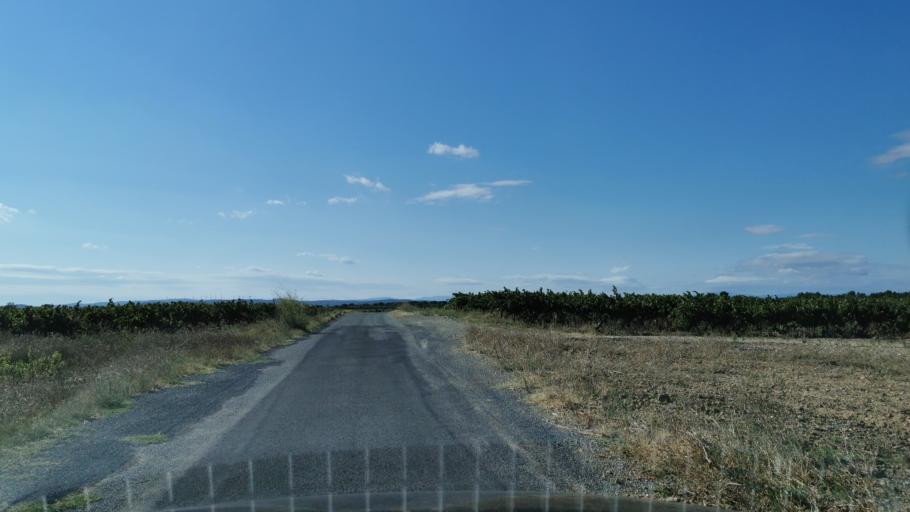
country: FR
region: Languedoc-Roussillon
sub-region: Departement de l'Aude
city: Ginestas
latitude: 43.2682
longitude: 2.8429
